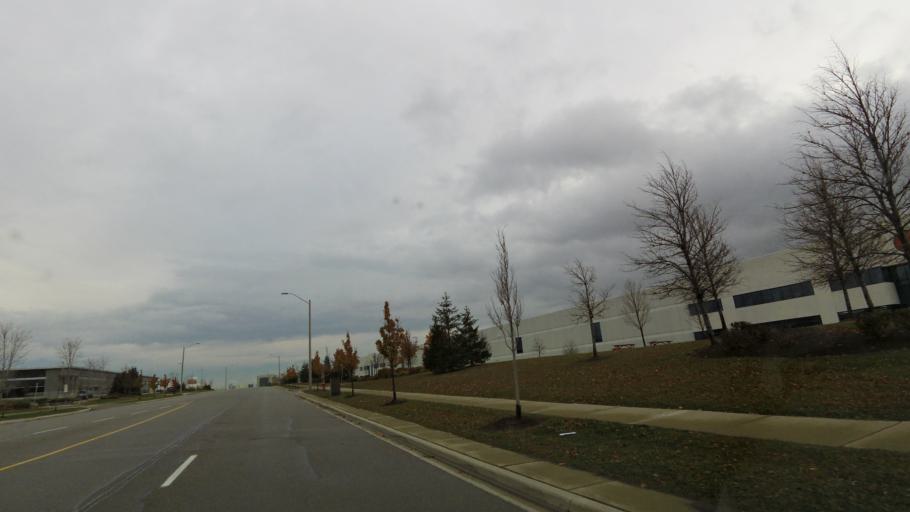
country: CA
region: Ontario
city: Mississauga
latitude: 43.6348
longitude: -79.6966
